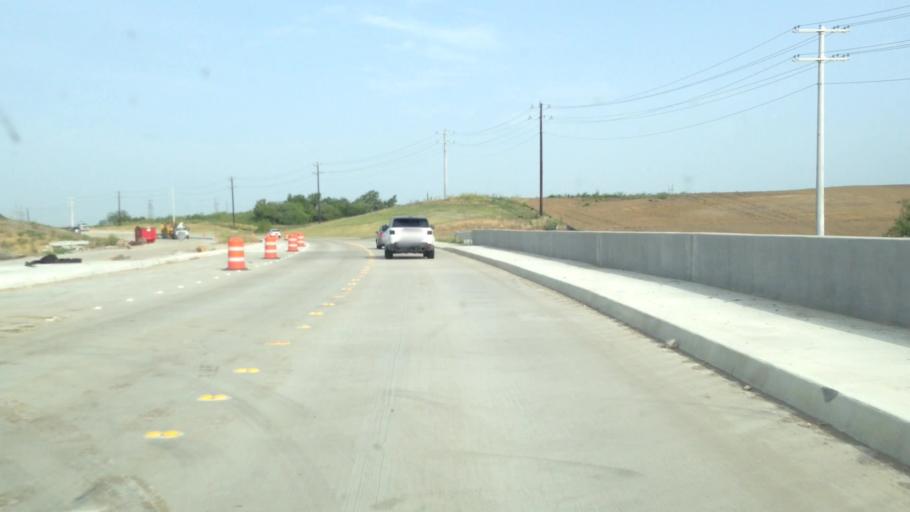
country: US
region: Texas
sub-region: Denton County
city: The Colony
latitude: 33.0471
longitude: -96.8947
